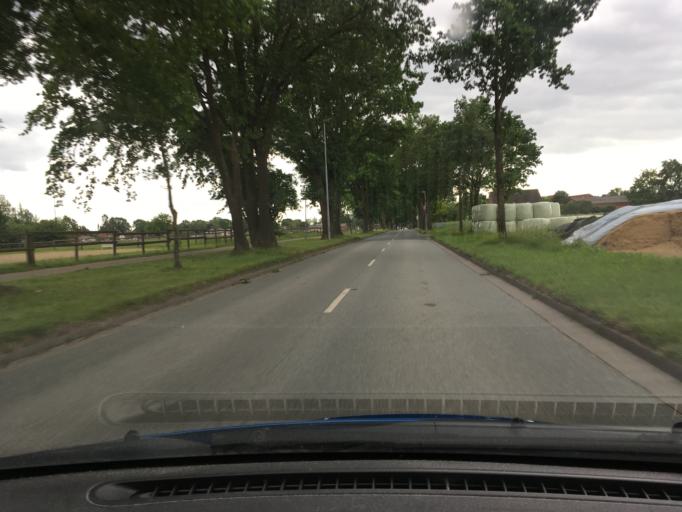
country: DE
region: Lower Saxony
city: Sittensen
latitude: 53.2870
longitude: 9.4999
